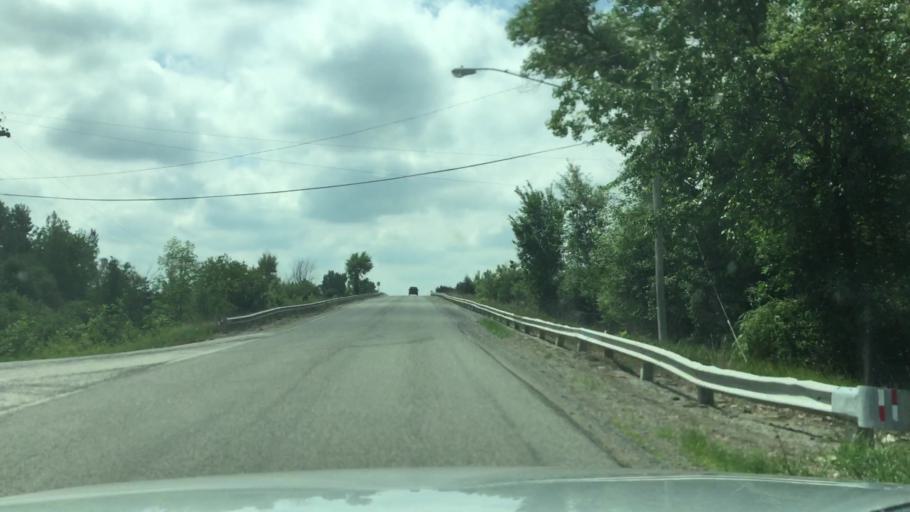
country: US
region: Michigan
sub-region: Saginaw County
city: Birch Run
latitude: 43.2711
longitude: -83.7944
